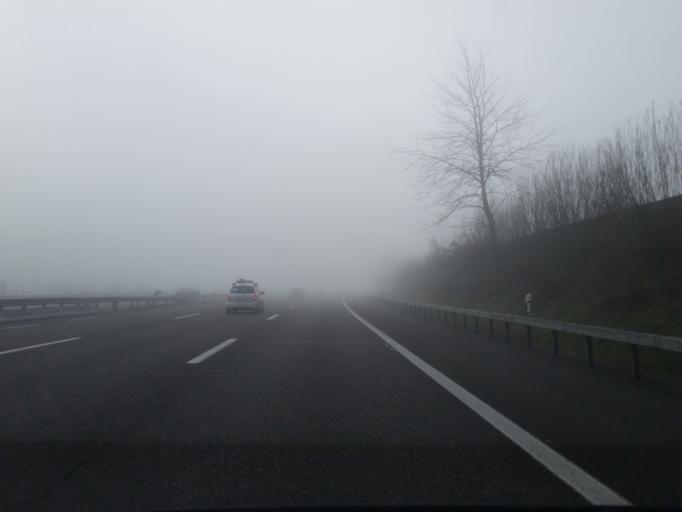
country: CH
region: Saint Gallen
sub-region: Wahlkreis Rorschach
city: Morschwil
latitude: 47.4613
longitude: 9.4366
